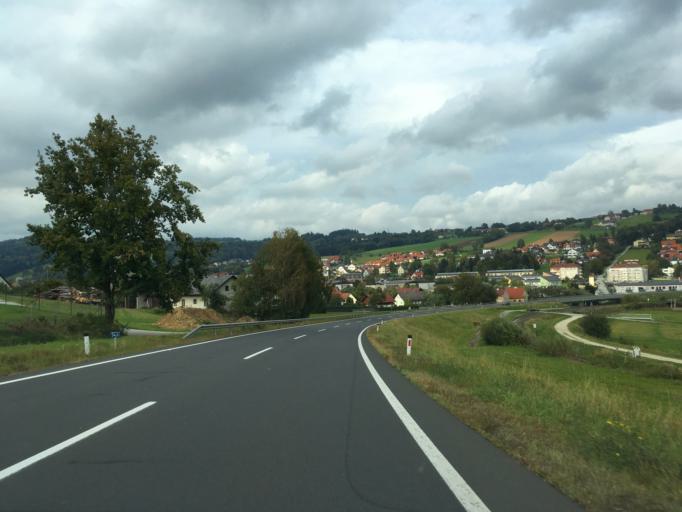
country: AT
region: Styria
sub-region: Politischer Bezirk Hartberg-Fuerstenfeld
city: Pinggau
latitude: 47.4360
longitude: 16.0657
